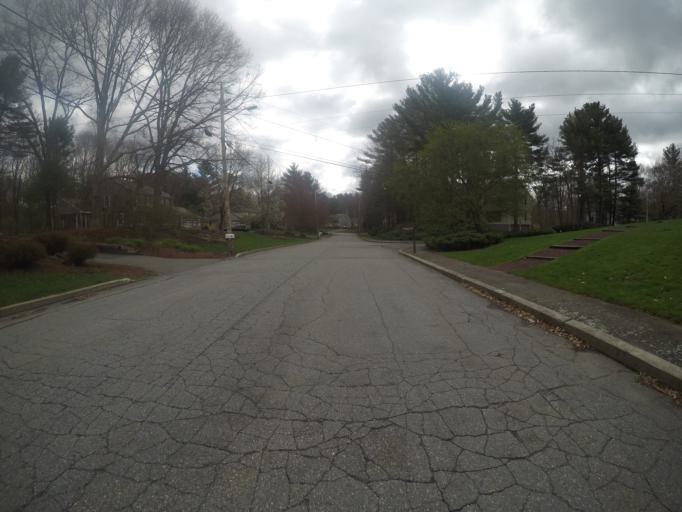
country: US
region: Massachusetts
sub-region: Bristol County
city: Easton
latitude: 42.0294
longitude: -71.1262
